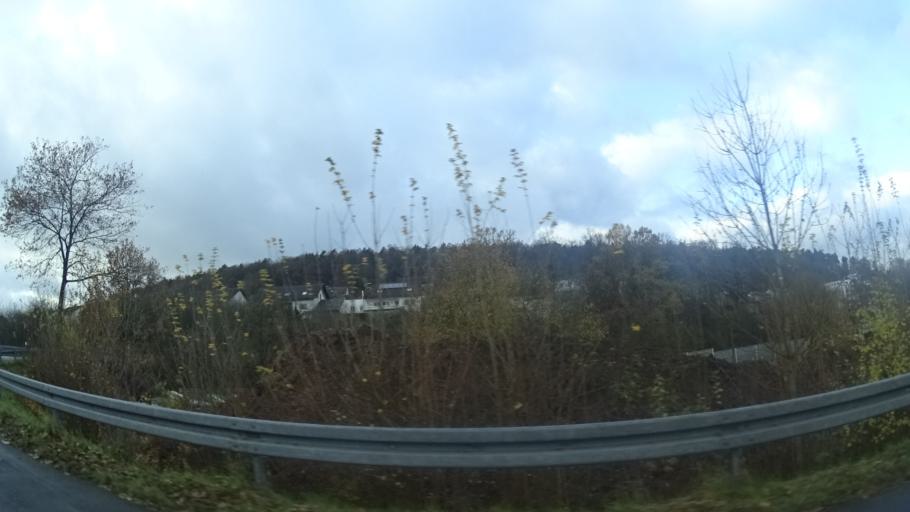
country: DE
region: Hesse
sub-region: Regierungsbezirk Kassel
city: Petersberg
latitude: 50.5842
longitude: 9.7304
